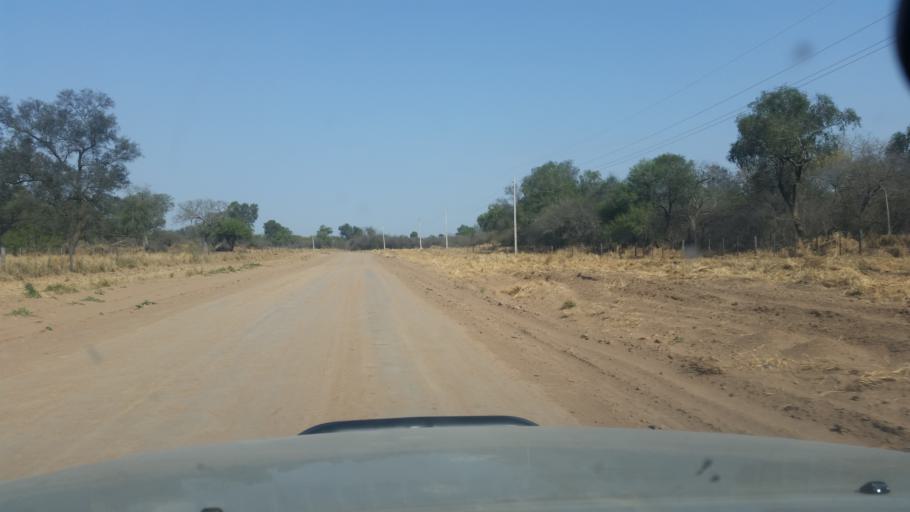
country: PY
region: Boqueron
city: Filadelfia
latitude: -22.0760
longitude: -60.6876
